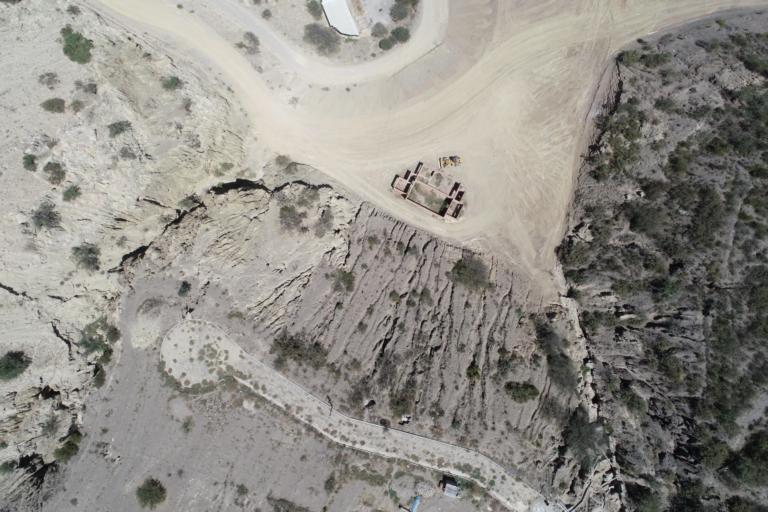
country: BO
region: La Paz
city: La Paz
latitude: -16.6163
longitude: -68.0602
